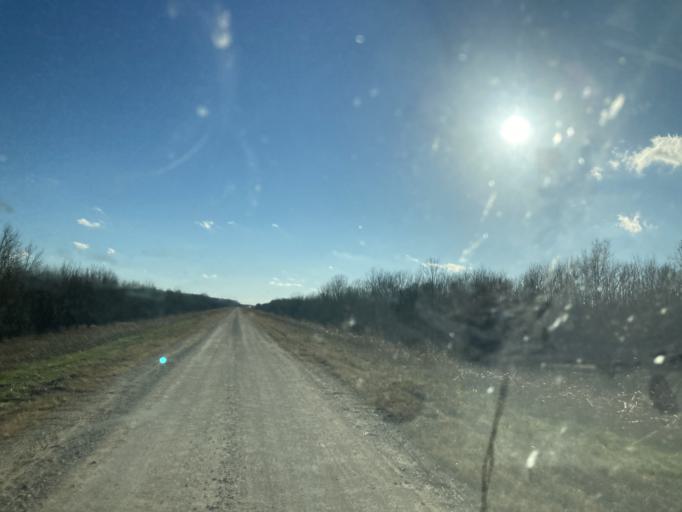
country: US
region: Mississippi
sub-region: Yazoo County
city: Yazoo City
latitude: 32.9296
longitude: -90.5492
